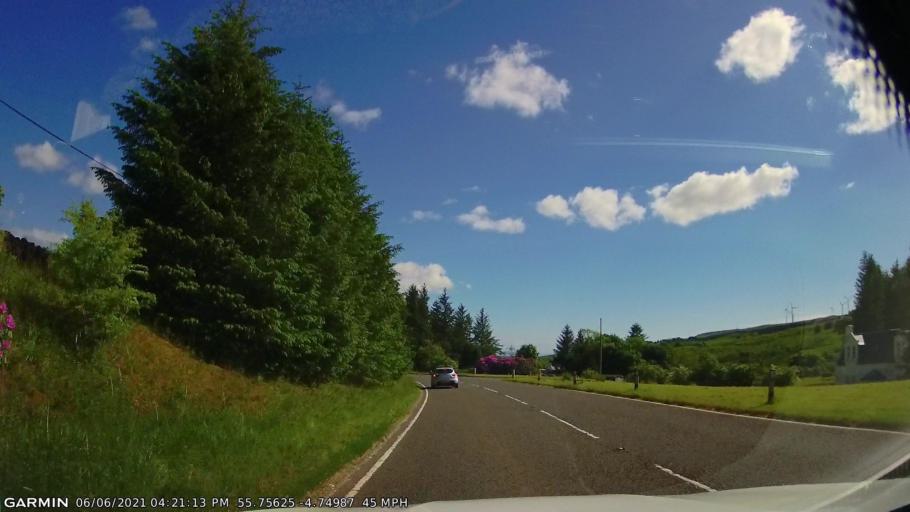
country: GB
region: Scotland
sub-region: North Ayrshire
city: Dalry
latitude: 55.7564
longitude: -4.7497
